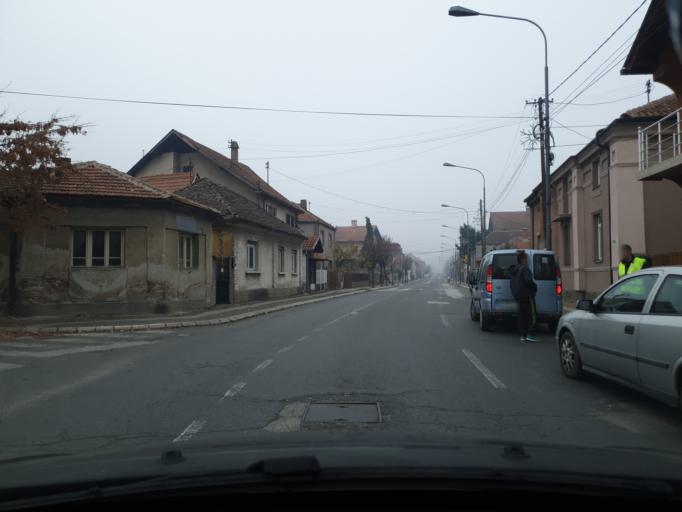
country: RS
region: Central Serbia
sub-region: Zajecarski Okrug
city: Zajecar
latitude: 43.9011
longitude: 22.2693
